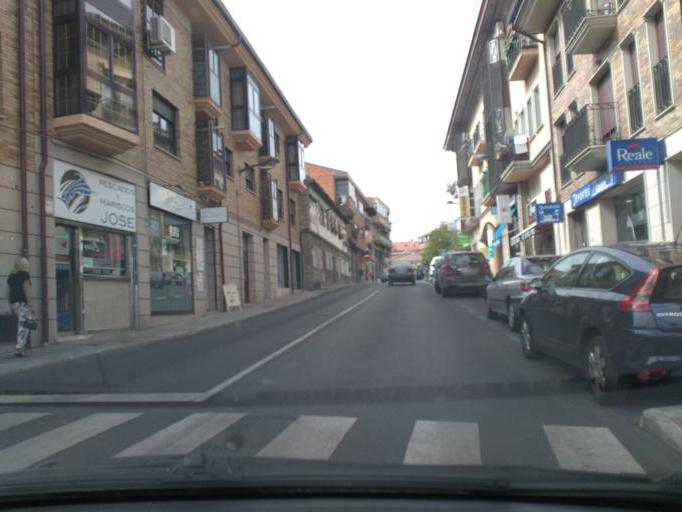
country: ES
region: Madrid
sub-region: Provincia de Madrid
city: Galapagar
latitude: 40.5758
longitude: -4.0032
